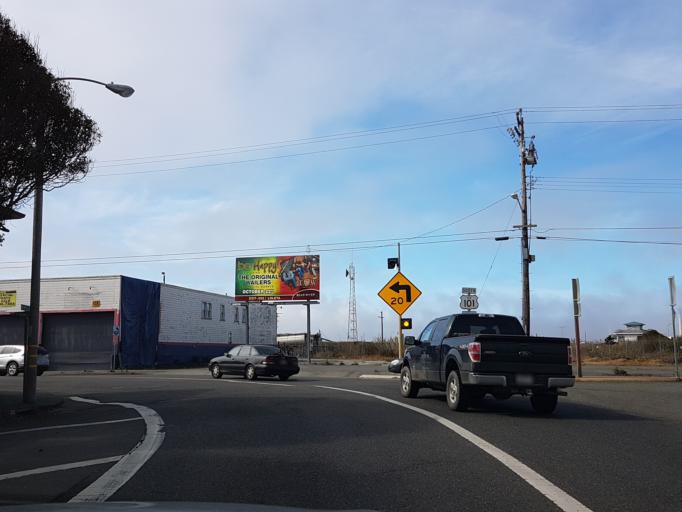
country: US
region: California
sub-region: Humboldt County
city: Eureka
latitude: 40.8016
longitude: -124.1747
